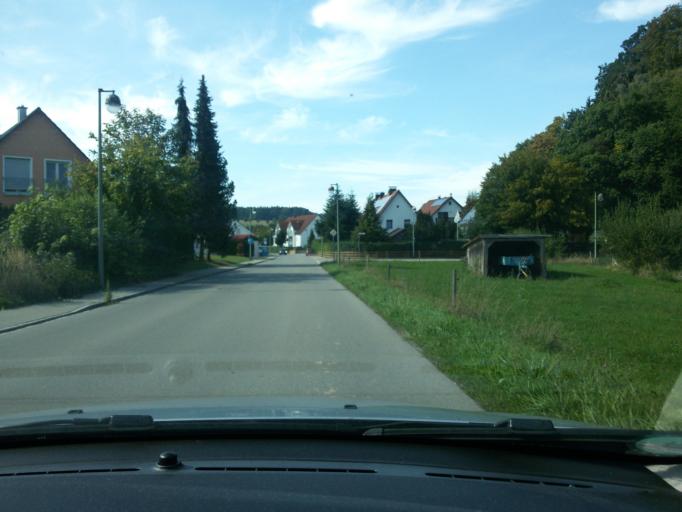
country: DE
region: Bavaria
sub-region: Swabia
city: Mickhausen
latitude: 48.2432
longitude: 10.6424
